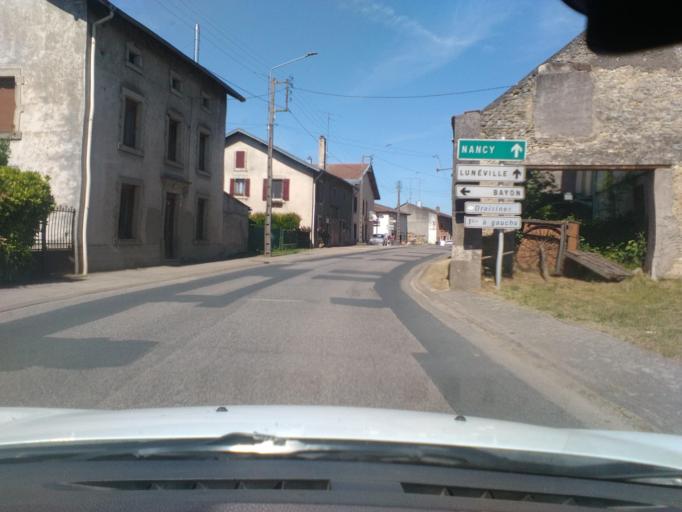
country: FR
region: Lorraine
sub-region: Departement de Meurthe-et-Moselle
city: Gerbeviller
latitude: 48.4455
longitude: 6.5652
